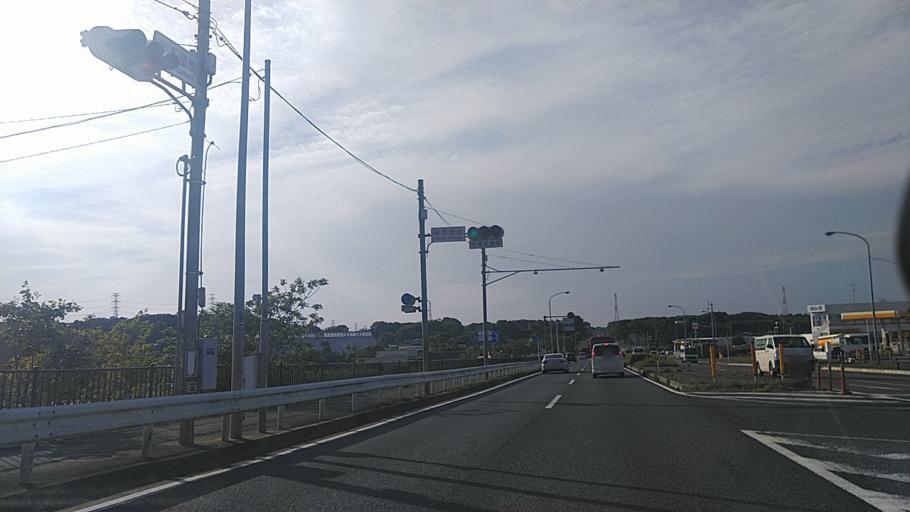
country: JP
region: Chiba
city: Shiroi
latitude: 35.7573
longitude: 140.1094
